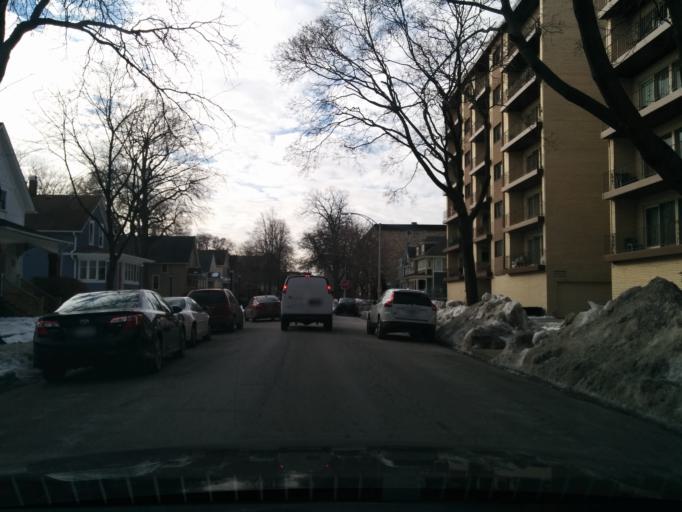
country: US
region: Illinois
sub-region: Cook County
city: Forest Park
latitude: 41.8821
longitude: -87.8074
